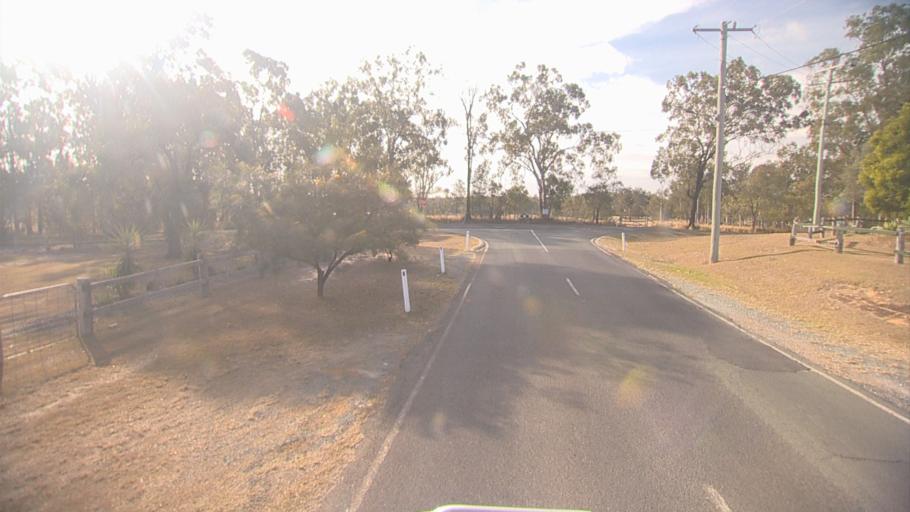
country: AU
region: Queensland
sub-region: Logan
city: Cedar Vale
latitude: -27.8655
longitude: 153.0057
